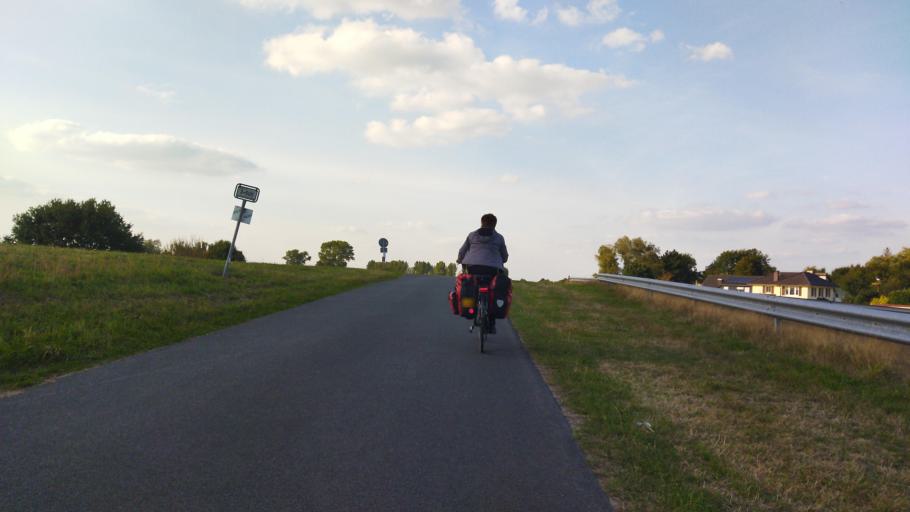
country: DE
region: Lower Saxony
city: Lehe
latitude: 53.0466
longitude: 7.3190
